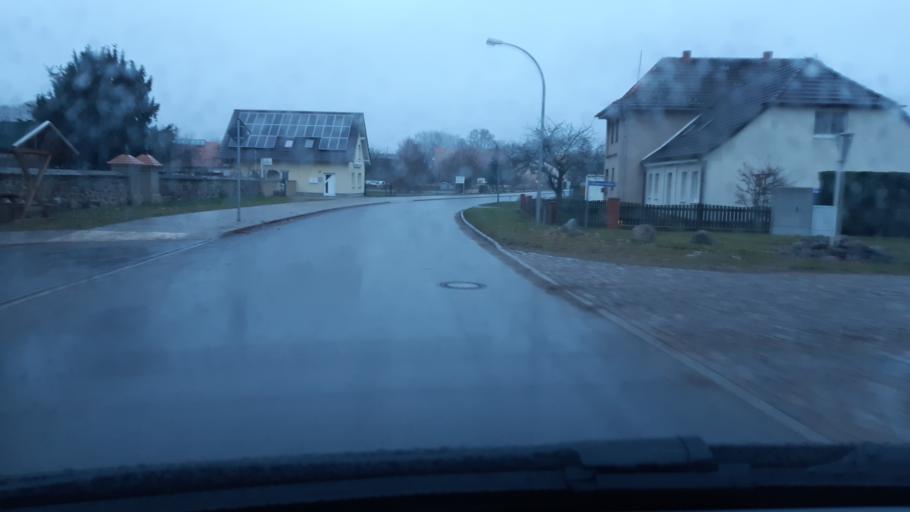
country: DE
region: Brandenburg
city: Milmersdorf
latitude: 53.1116
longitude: 13.6415
